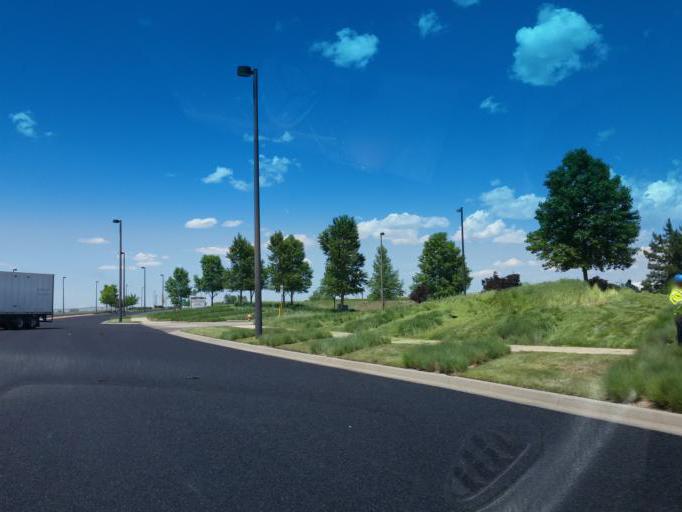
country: US
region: Colorado
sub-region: Larimer County
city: Loveland
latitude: 40.4312
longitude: -105.0013
